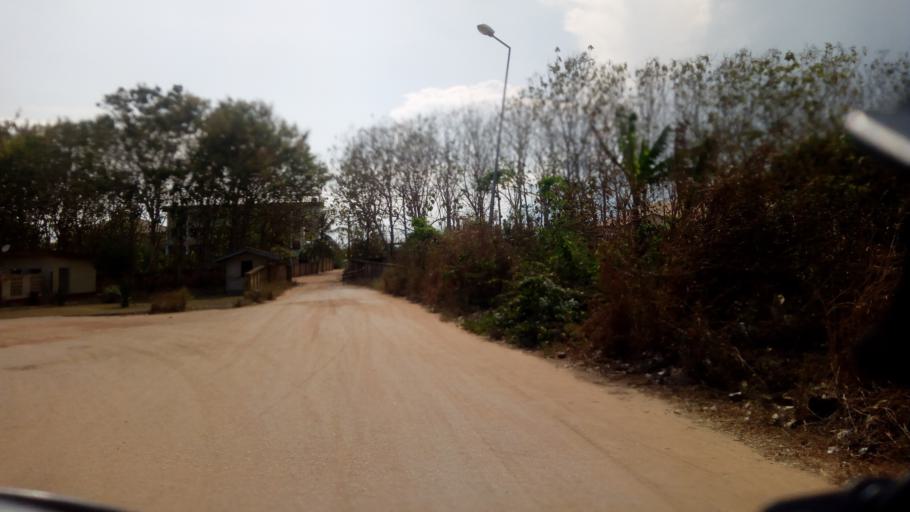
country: GH
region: Central
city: Cape Coast
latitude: 5.1263
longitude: -1.2944
